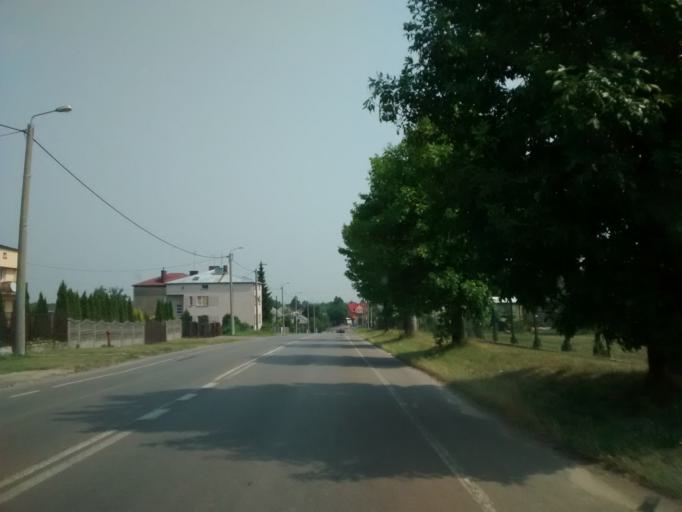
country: PL
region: Silesian Voivodeship
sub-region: Powiat zawiercianski
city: Ogrodzieniec
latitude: 50.4539
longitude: 19.5438
